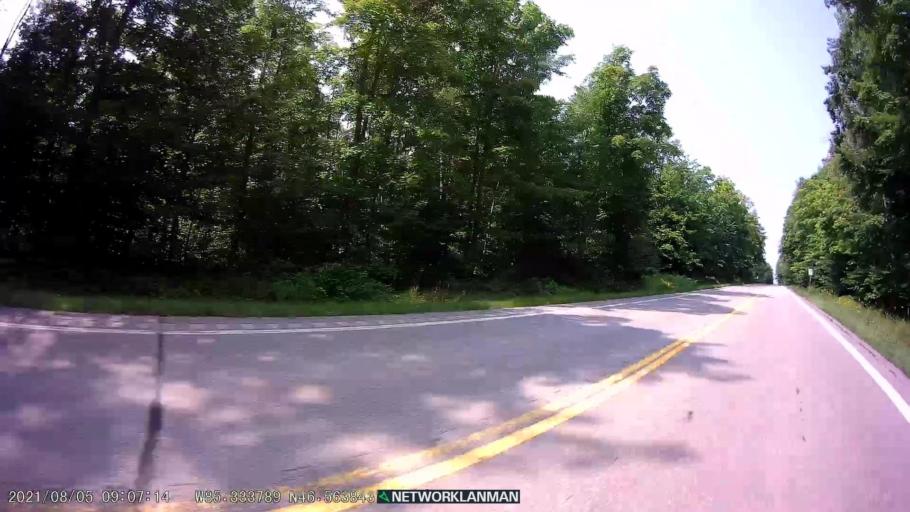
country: US
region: Michigan
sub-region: Luce County
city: Newberry
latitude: 46.5639
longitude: -85.3341
